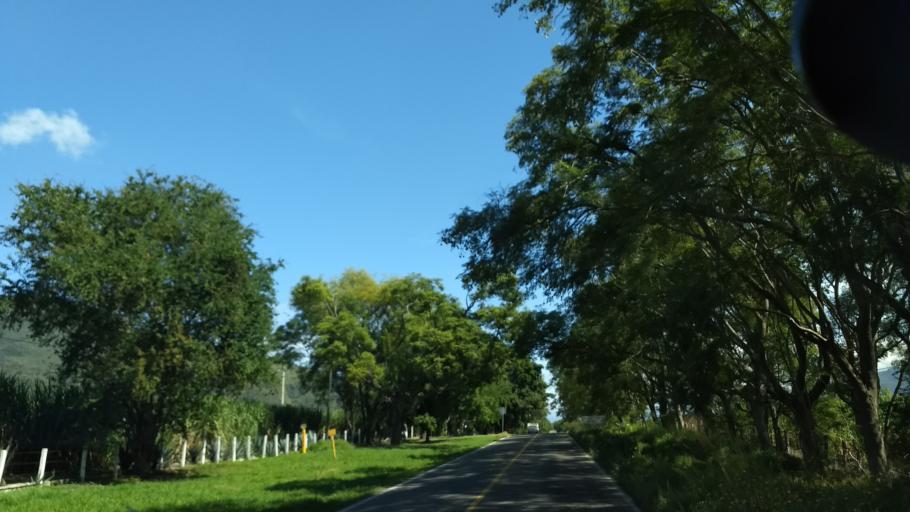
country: MX
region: Jalisco
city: Tuxpan
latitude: 19.5368
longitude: -103.4121
